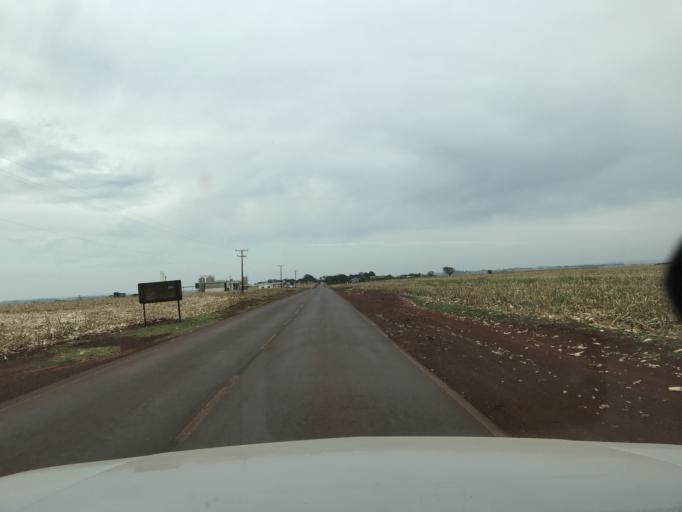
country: BR
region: Parana
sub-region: Palotina
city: Palotina
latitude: -24.4188
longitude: -53.8698
